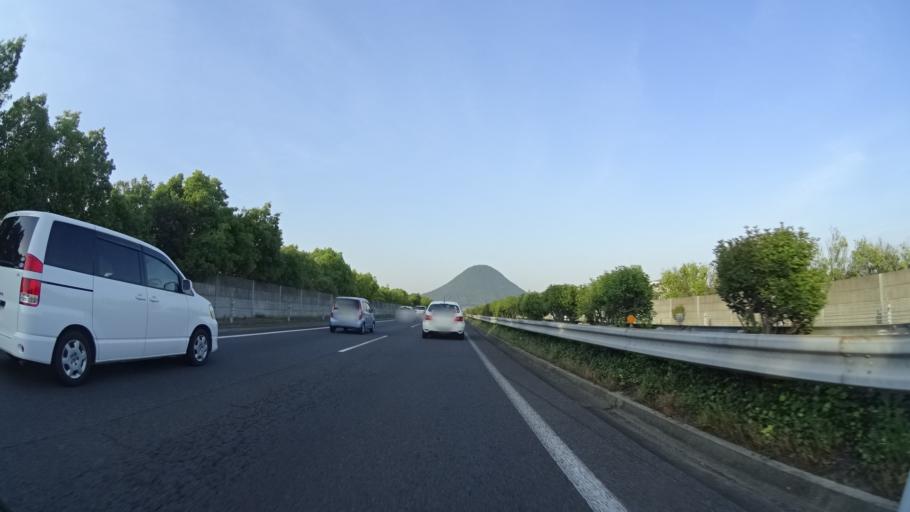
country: JP
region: Kagawa
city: Marugame
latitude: 34.2576
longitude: 133.8087
